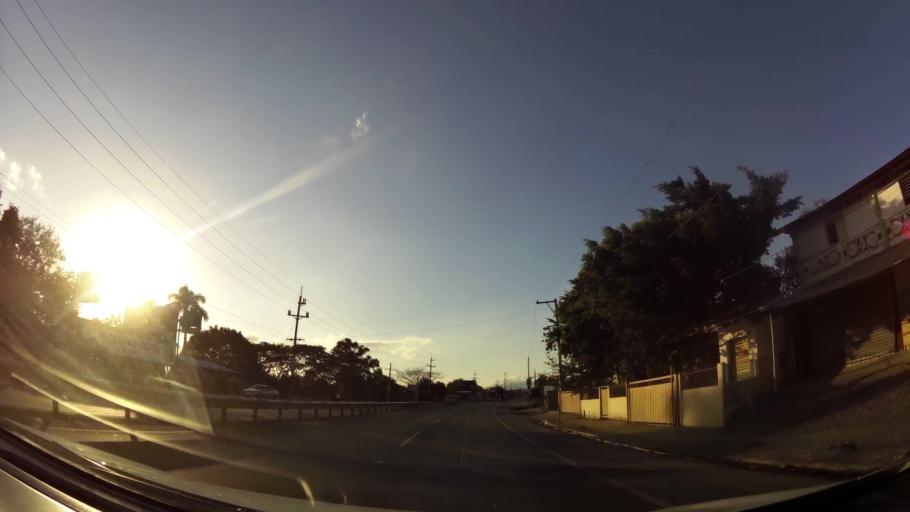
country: DO
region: Santiago
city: Palmar Arriba
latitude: 19.5051
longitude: -70.7523
